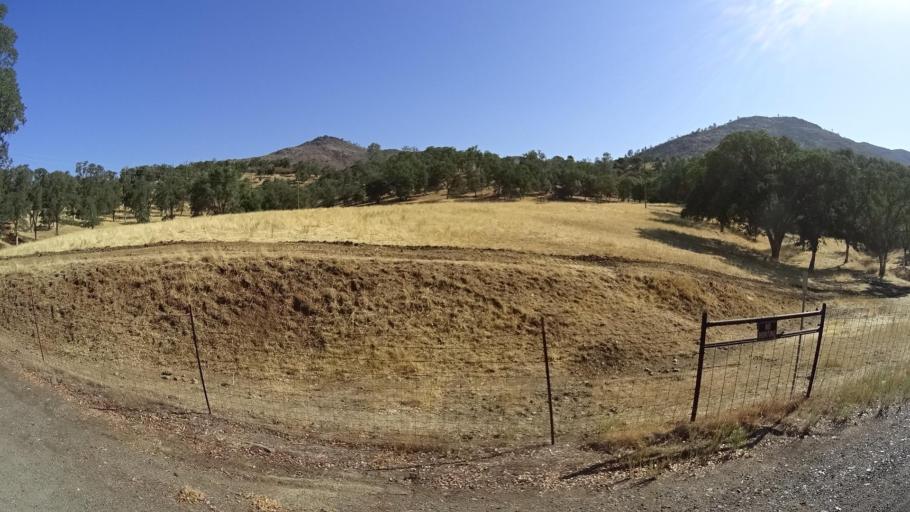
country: US
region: California
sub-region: Mariposa County
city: Mariposa
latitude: 37.5805
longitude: -120.1743
